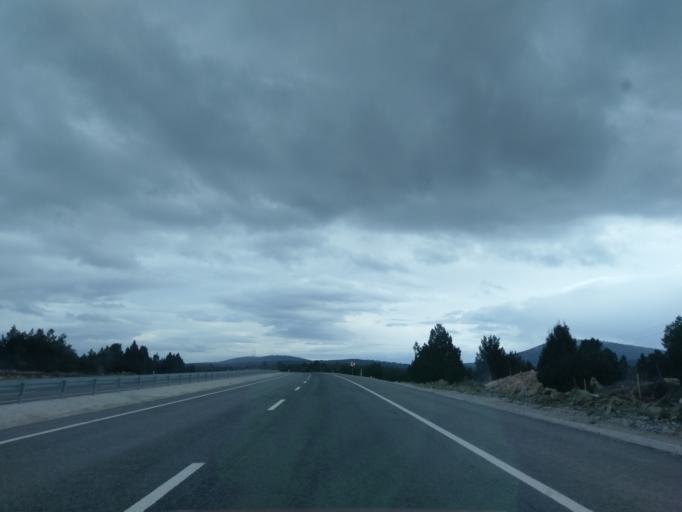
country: TR
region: Kuetahya
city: Cavdarhisar
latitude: 39.2229
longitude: 29.7329
